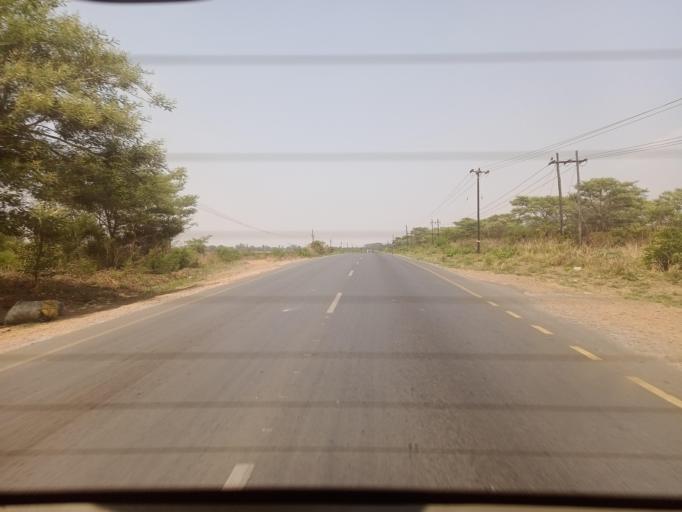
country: ZM
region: Lusaka
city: Lusaka
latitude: -15.2680
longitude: 28.4180
